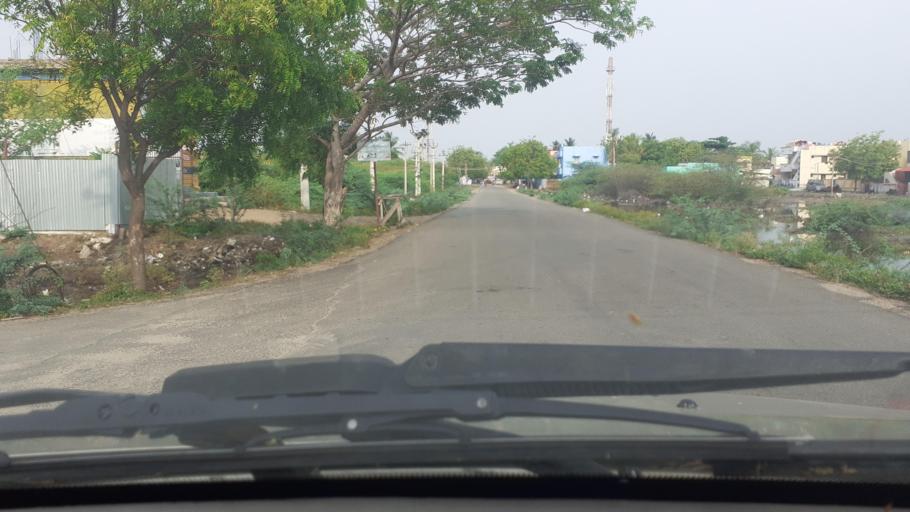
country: IN
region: Tamil Nadu
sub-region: Thoothukkudi
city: Korampallam
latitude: 8.7928
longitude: 78.1096
